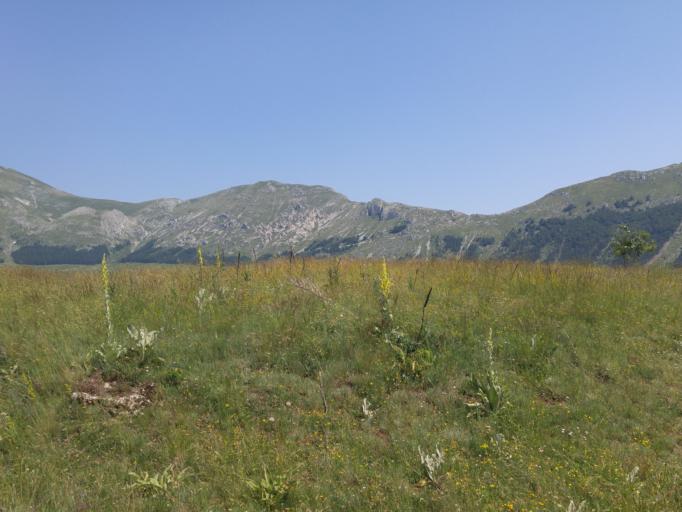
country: IT
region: Abruzzo
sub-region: Provincia dell' Aquila
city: Castel del Monte
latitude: 42.3992
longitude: 13.7546
